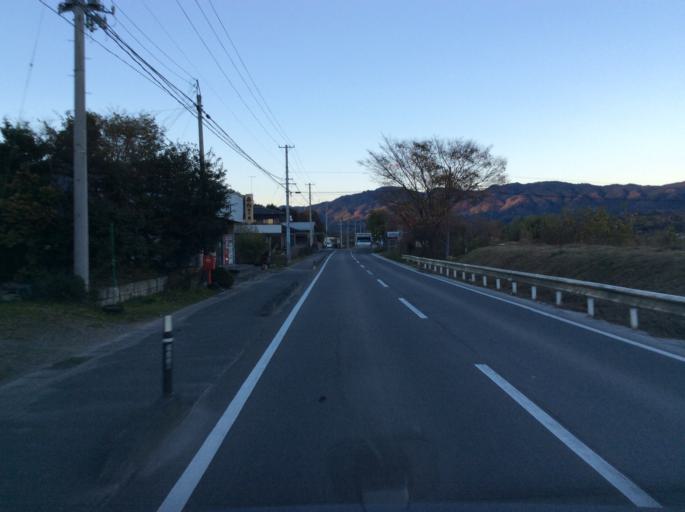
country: JP
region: Fukushima
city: Iwaki
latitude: 37.1055
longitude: 140.8624
